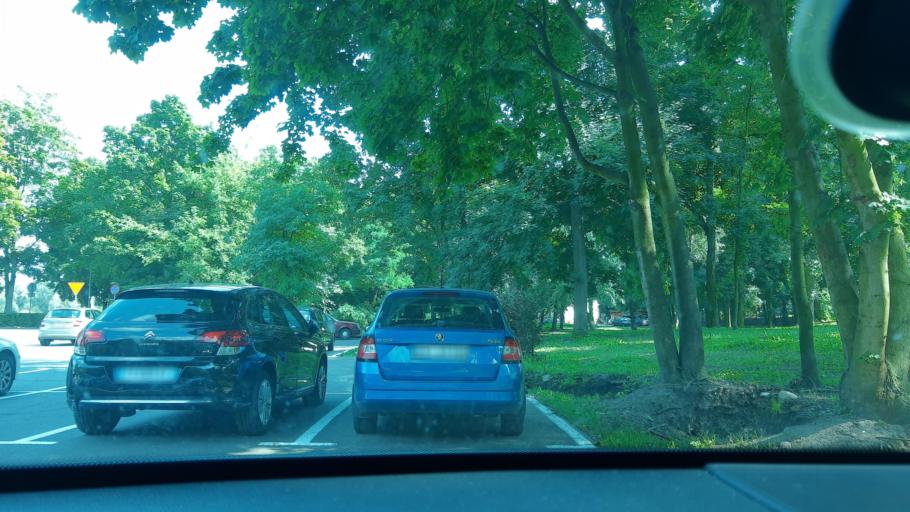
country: PL
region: Lodz Voivodeship
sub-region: Powiat sieradzki
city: Sieradz
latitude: 51.5996
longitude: 18.7404
